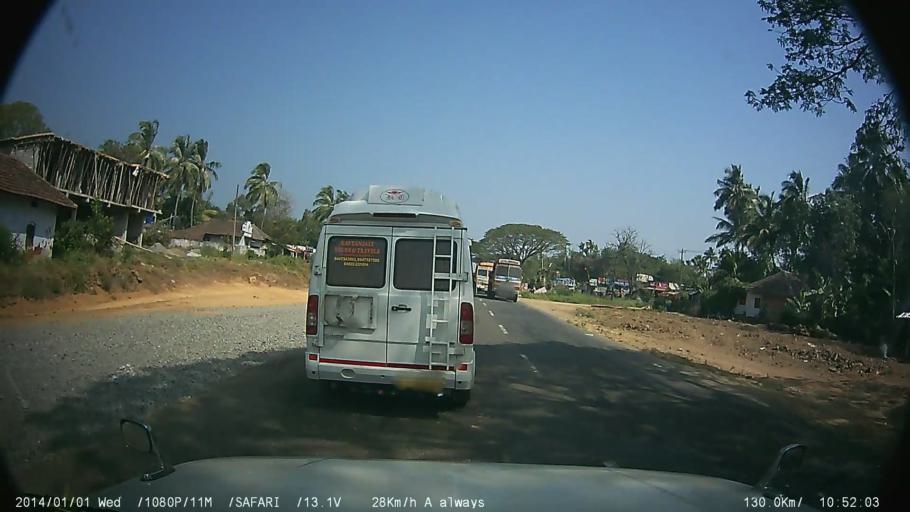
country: IN
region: Kerala
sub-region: Palakkad district
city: Palakkad
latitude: 10.7077
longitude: 76.5946
